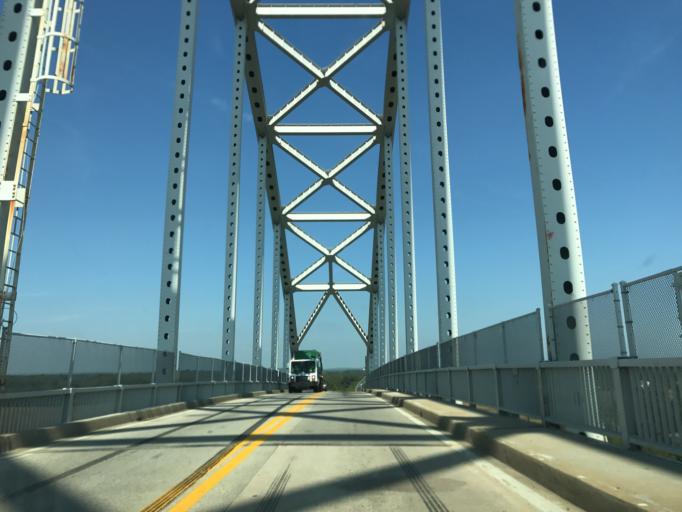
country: US
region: Maryland
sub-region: Cecil County
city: Elkton
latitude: 39.5288
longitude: -75.8141
